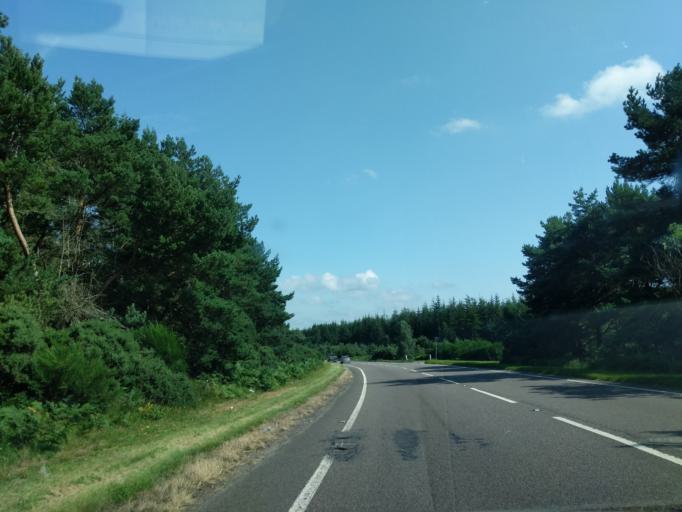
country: GB
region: Scotland
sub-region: Moray
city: Lhanbryd
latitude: 57.6282
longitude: -3.1687
